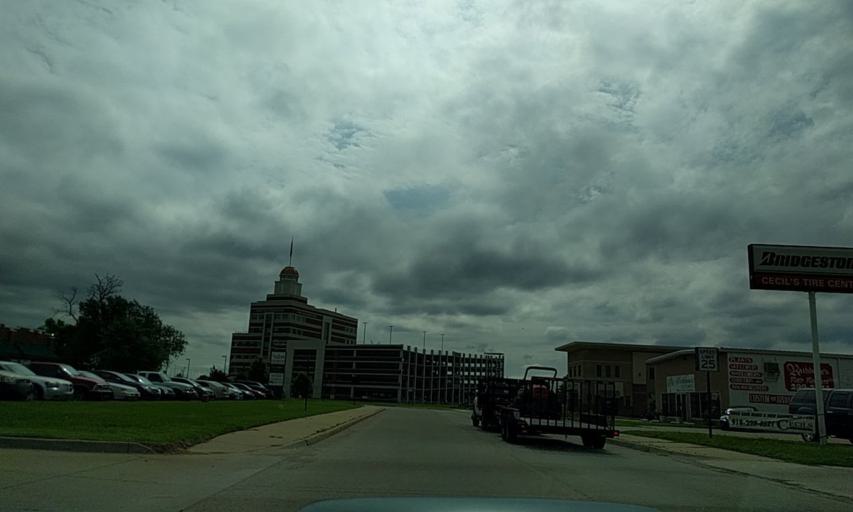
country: US
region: Oklahoma
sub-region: Tulsa County
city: Jenks
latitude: 36.0226
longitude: -95.9633
